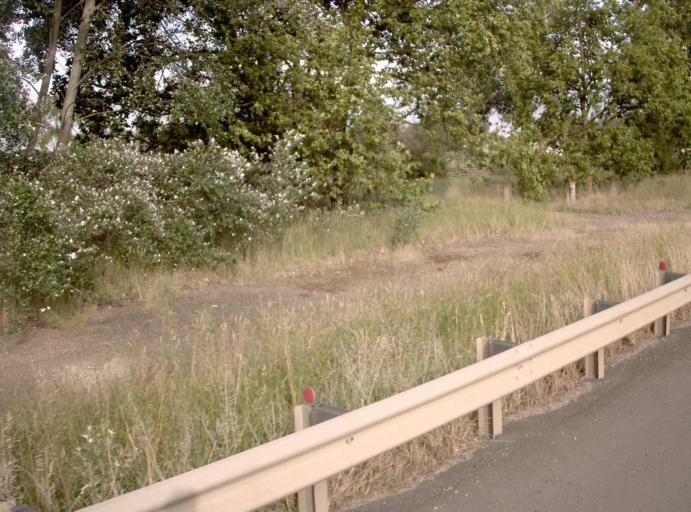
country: AU
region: Victoria
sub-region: Wellington
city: Heyfield
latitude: -37.9635
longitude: 146.8989
